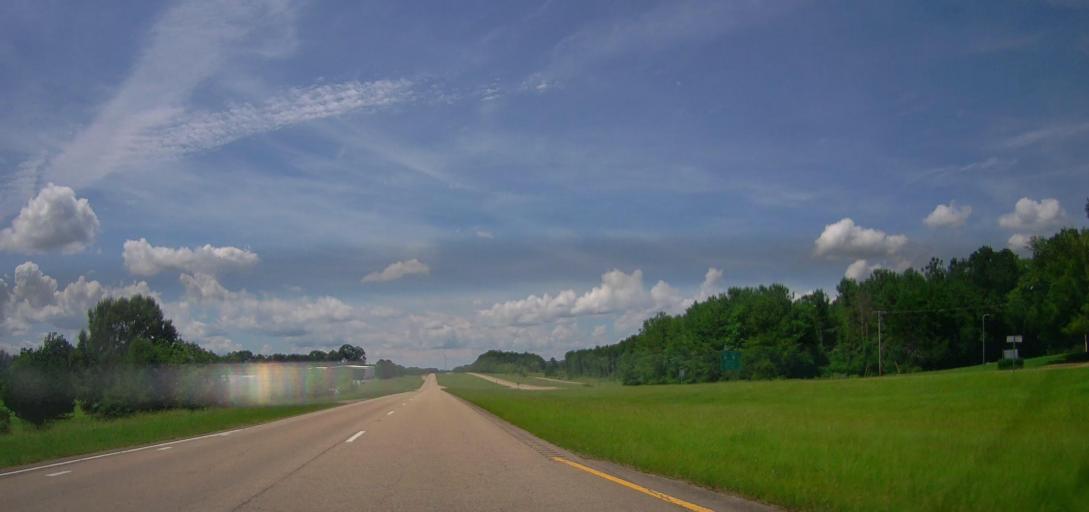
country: US
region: Mississippi
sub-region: Lee County
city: Nettleton
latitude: 33.9870
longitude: -88.6209
